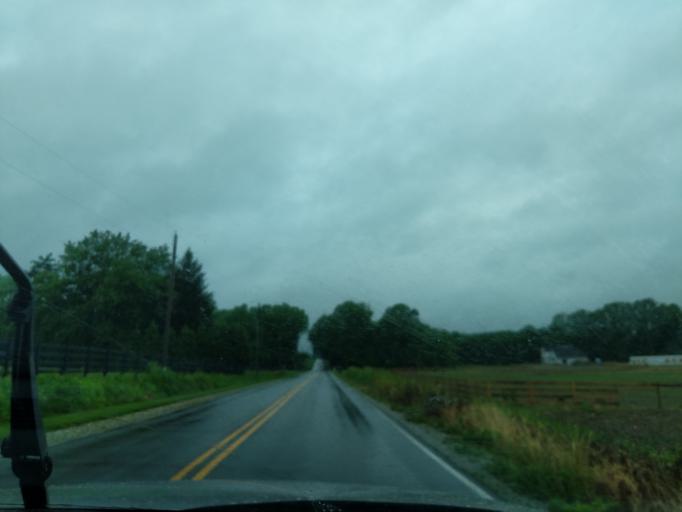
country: US
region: Indiana
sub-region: Madison County
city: Lapel
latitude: 40.0669
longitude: -85.8924
